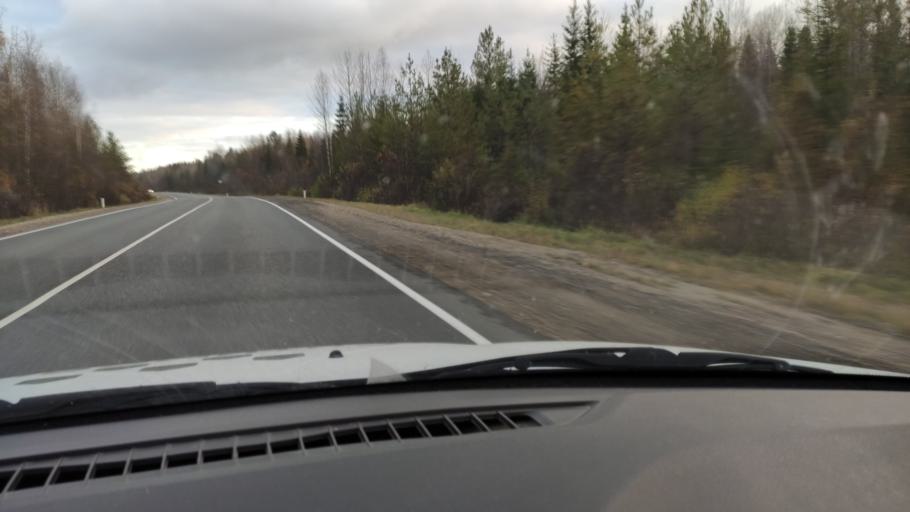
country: RU
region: Kirov
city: Omutninsk
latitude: 58.7096
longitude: 52.0993
